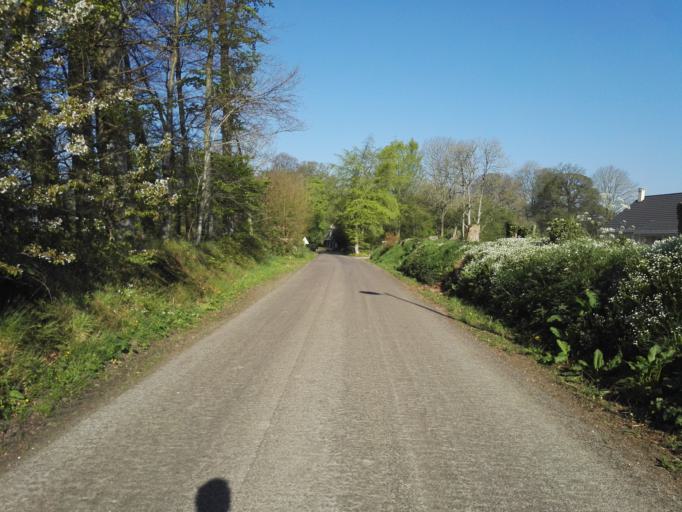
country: FR
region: Haute-Normandie
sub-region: Departement de la Seine-Maritime
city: Doudeville
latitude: 49.7372
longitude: 0.7149
